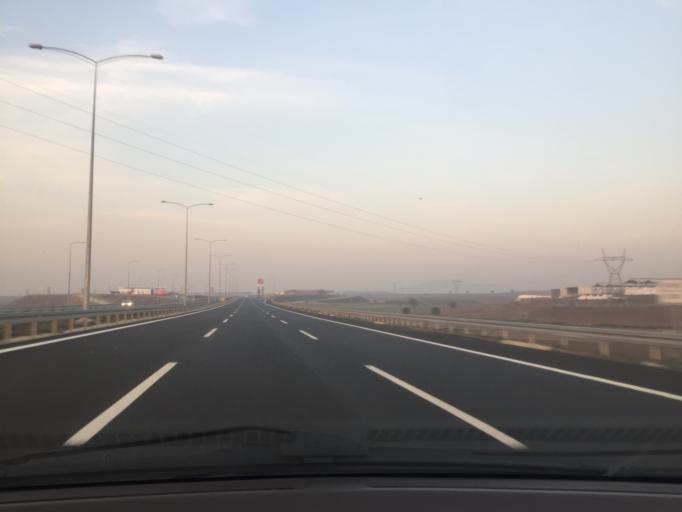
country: TR
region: Bursa
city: Karacabey
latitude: 40.2537
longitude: 28.4625
